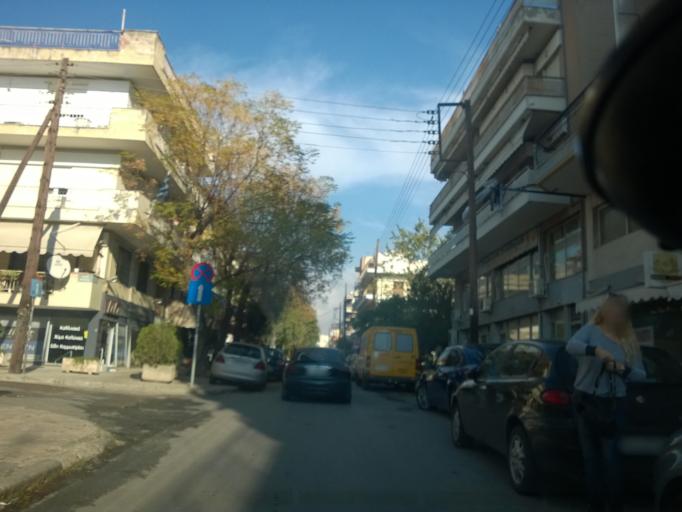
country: GR
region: Central Macedonia
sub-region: Nomos Thessalonikis
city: Stavroupoli
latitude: 40.6739
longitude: 22.9276
